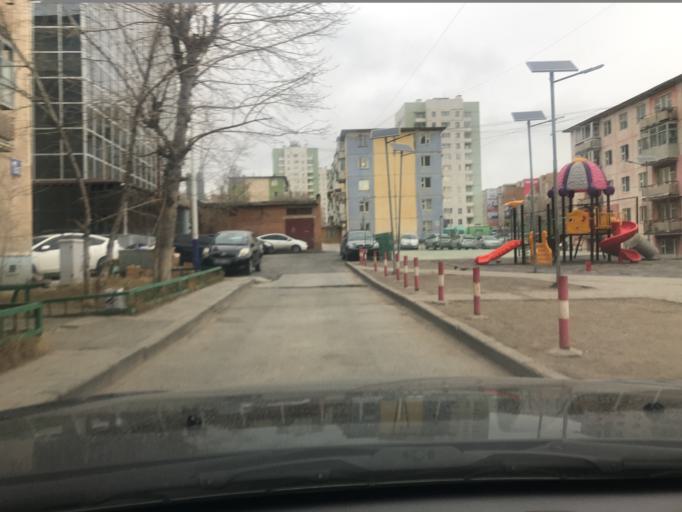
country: MN
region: Ulaanbaatar
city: Ulaanbaatar
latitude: 47.9213
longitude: 106.9414
